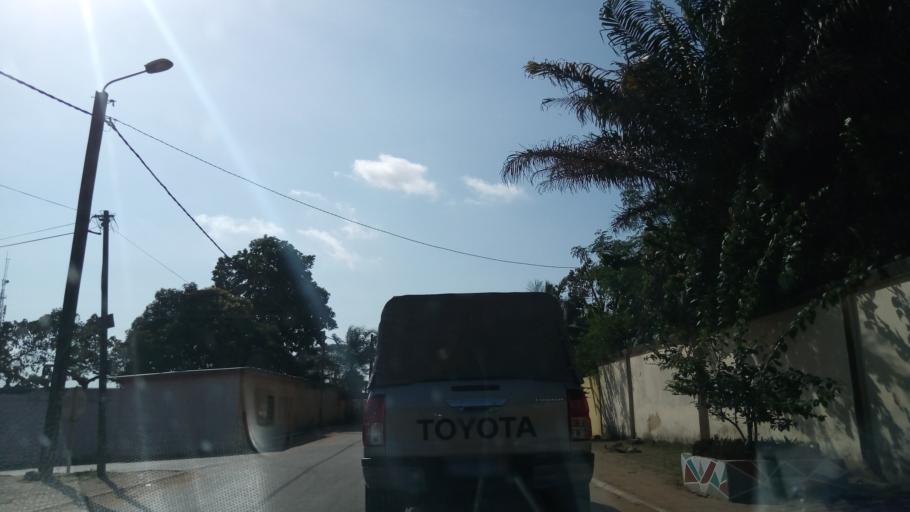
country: CI
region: Lagunes
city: Bingerville
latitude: 5.3598
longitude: -3.8884
